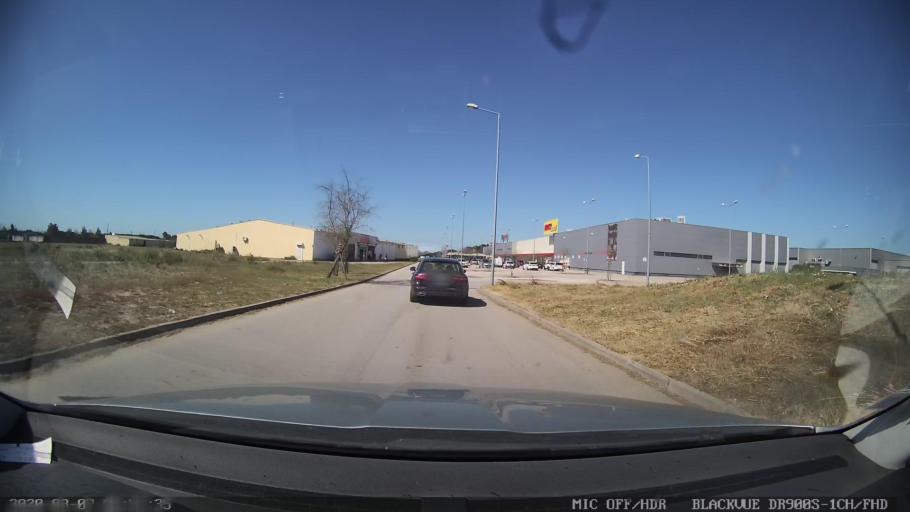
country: PT
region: Santarem
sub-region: Benavente
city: Benavente
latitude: 38.9599
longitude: -8.8174
